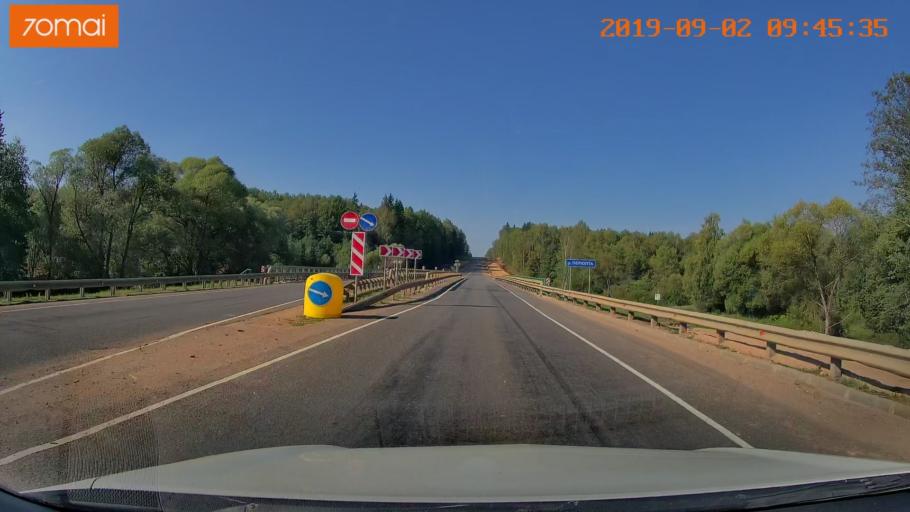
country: RU
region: Kaluga
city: Mosal'sk
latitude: 54.6353
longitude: 34.8463
